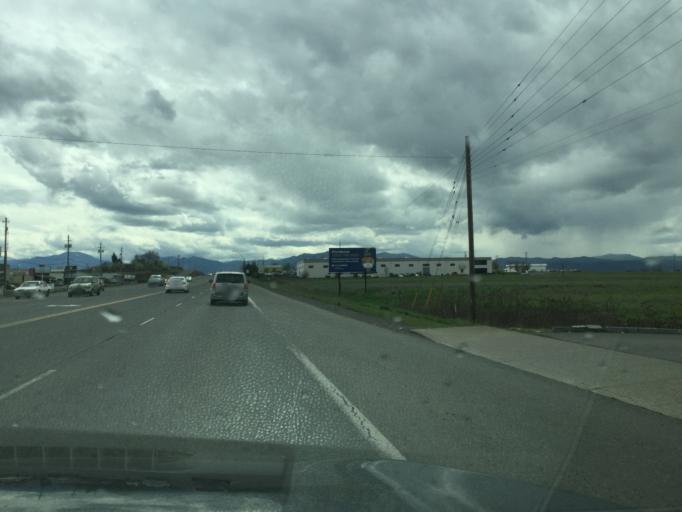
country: US
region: Oregon
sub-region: Jackson County
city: White City
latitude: 42.3890
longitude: -122.8560
